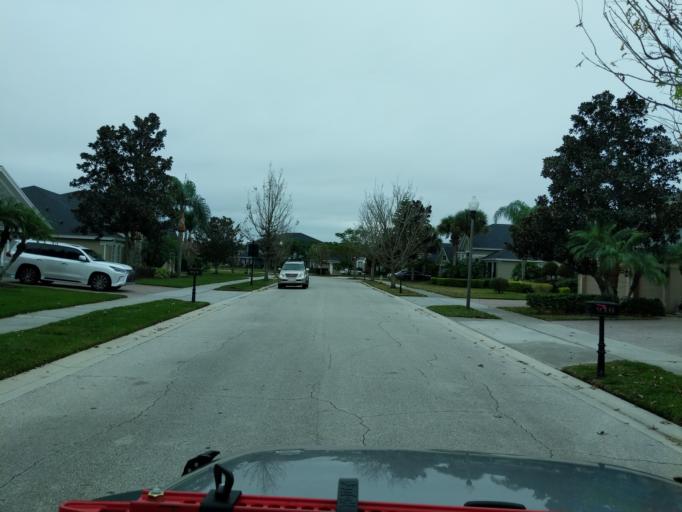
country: US
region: Florida
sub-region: Orange County
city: Winter Garden
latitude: 28.5291
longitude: -81.5812
